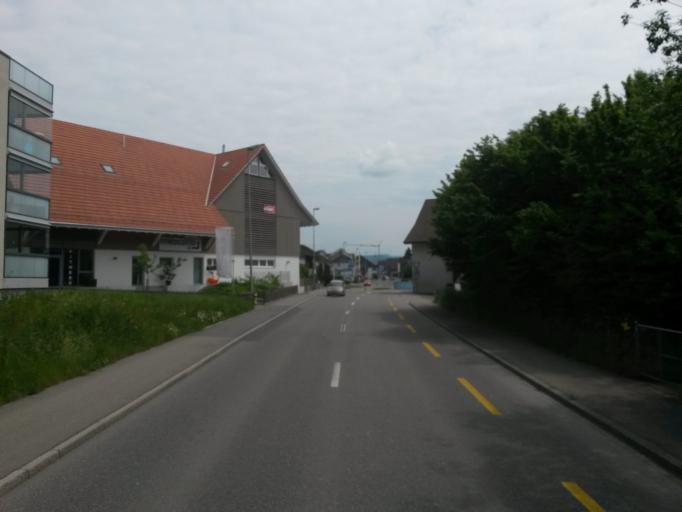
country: CH
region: Zurich
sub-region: Bezirk Pfaeffikon
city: Fehraltorf
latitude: 47.3905
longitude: 8.7470
